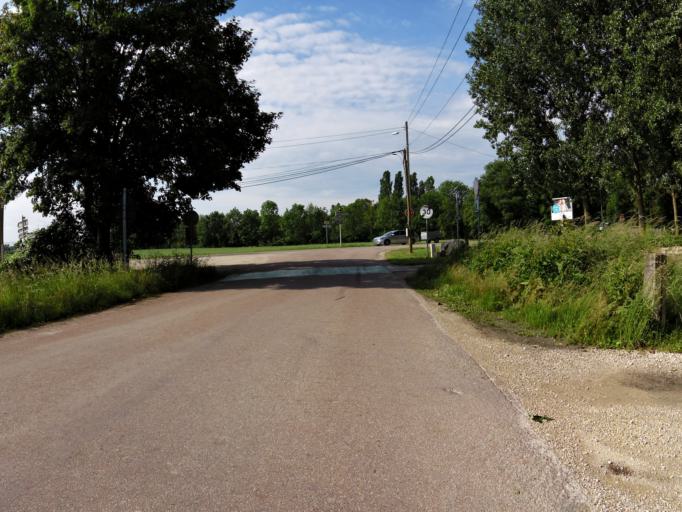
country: FR
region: Champagne-Ardenne
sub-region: Departement de l'Aube
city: Saint-Julien-les-Villas
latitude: 48.2697
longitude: 4.1100
